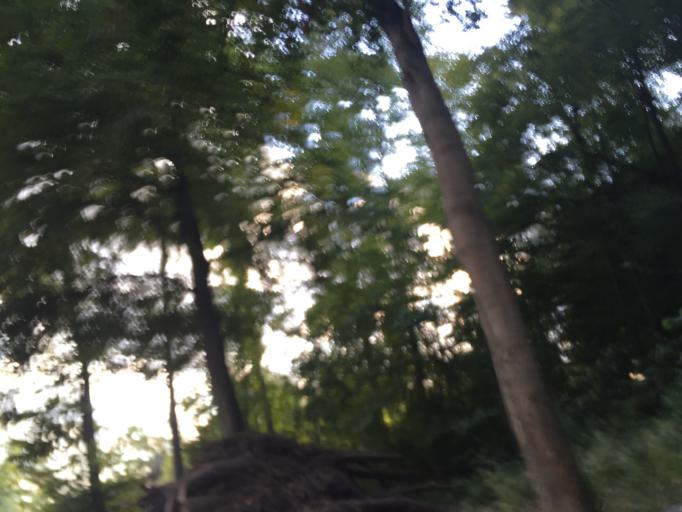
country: CH
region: Bern
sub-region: Bern-Mittelland District
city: Bern
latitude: 46.9637
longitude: 7.4364
